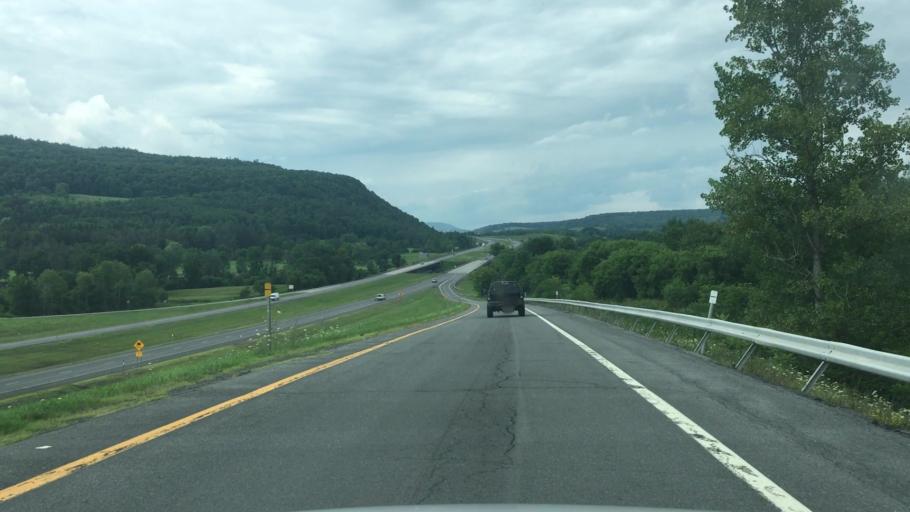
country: US
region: New York
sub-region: Schoharie County
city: Schoharie
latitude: 42.7077
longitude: -74.3150
